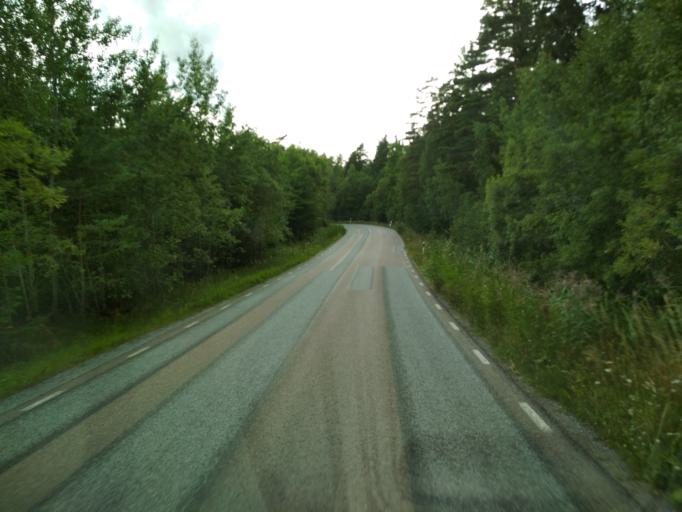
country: SE
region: Uppsala
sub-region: Habo Kommun
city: Balsta
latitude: 59.6760
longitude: 17.5796
